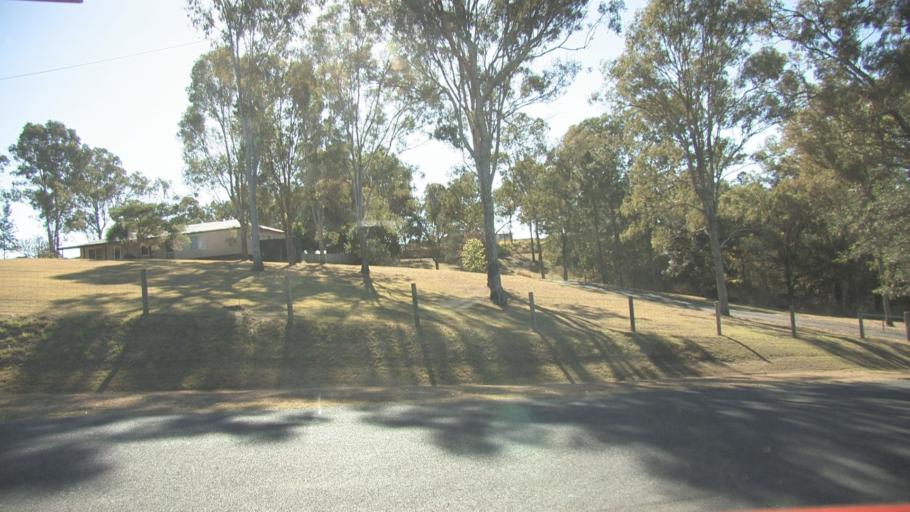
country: AU
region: Queensland
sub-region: Logan
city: Cedar Vale
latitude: -27.8928
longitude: 152.9789
